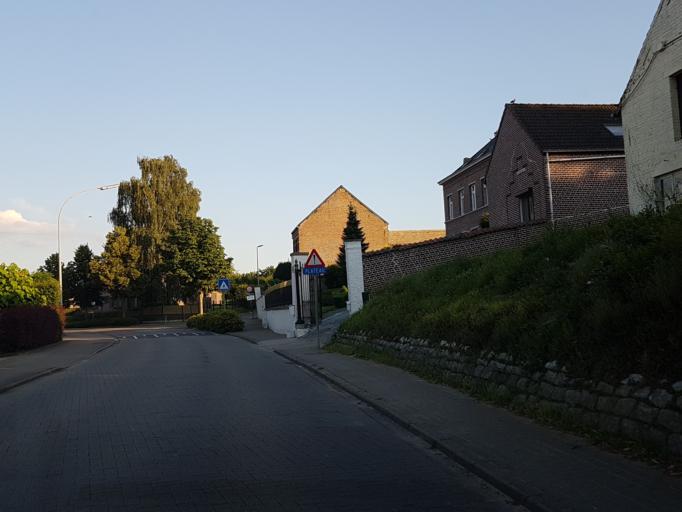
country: BE
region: Flanders
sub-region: Provincie Vlaams-Brabant
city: Merchtem
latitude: 50.9296
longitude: 4.2275
